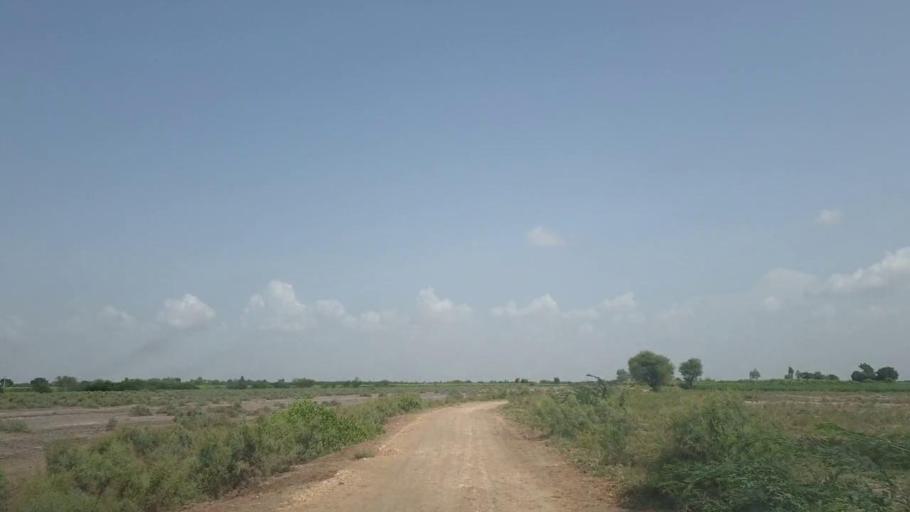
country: PK
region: Sindh
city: Tando Bago
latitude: 24.7528
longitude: 69.1752
